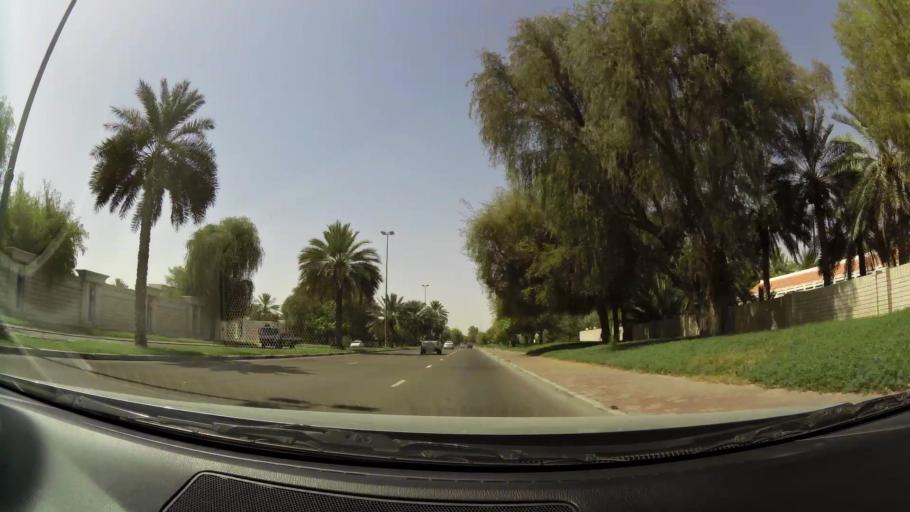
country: OM
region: Al Buraimi
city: Al Buraymi
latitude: 24.2926
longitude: 55.7677
